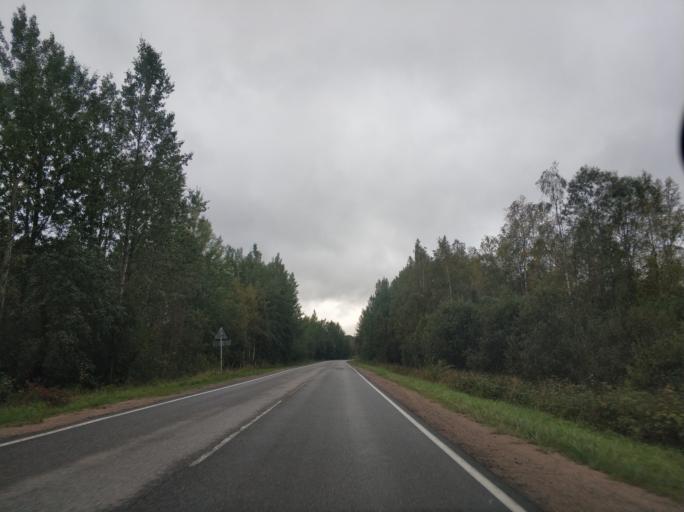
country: RU
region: Leningrad
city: Borisova Griva
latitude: 60.1175
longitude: 30.9637
